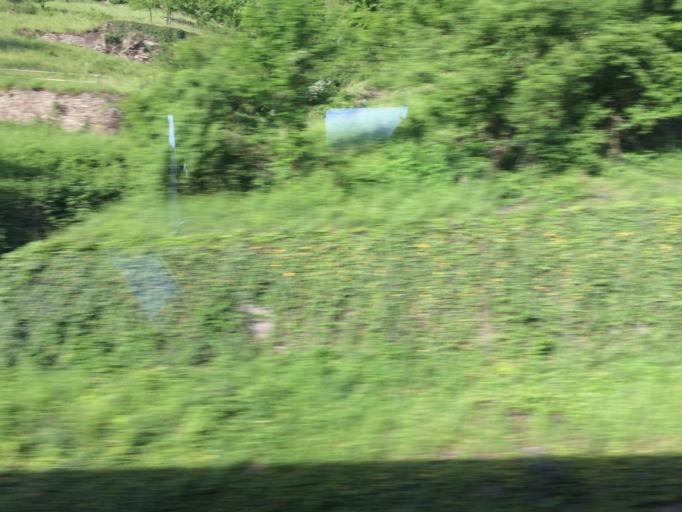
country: DE
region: Rheinland-Pfalz
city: Dorscheid
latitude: 50.0974
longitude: 7.7501
